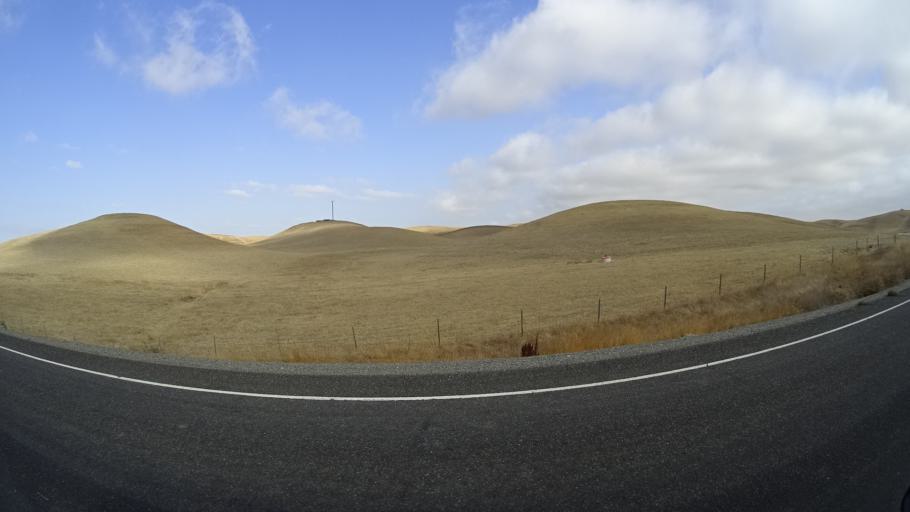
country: US
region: California
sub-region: Yolo County
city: Esparto
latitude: 38.7768
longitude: -121.9489
